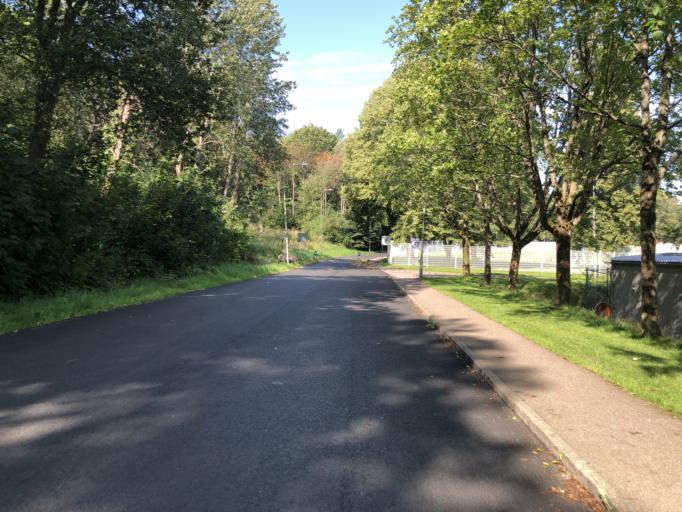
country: SE
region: Vaestra Goetaland
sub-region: Goteborg
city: Goeteborg
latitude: 57.7432
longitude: 11.9661
